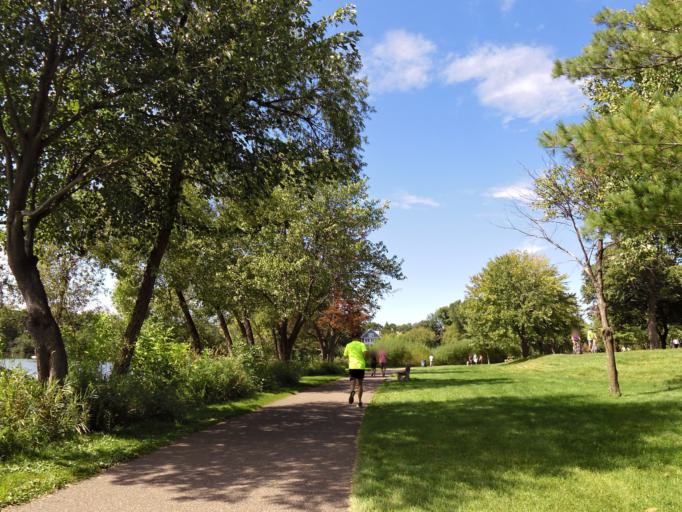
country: US
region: Minnesota
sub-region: Hennepin County
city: Saint Louis Park
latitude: 44.9561
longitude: -93.3032
